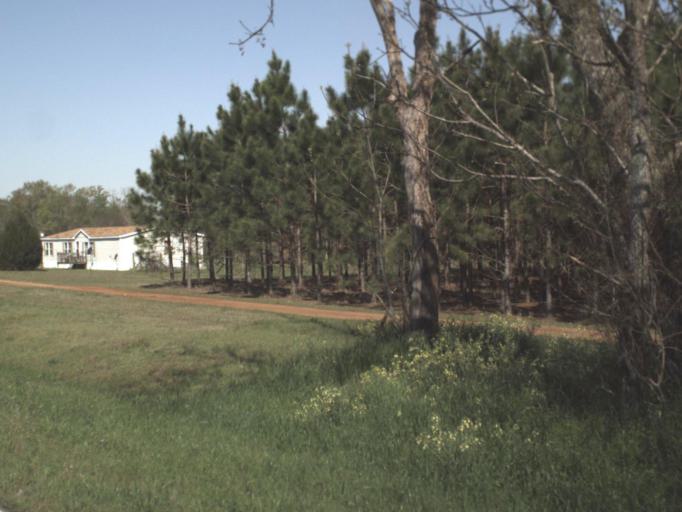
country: US
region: Florida
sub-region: Jackson County
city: Graceville
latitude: 30.9531
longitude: -85.4340
